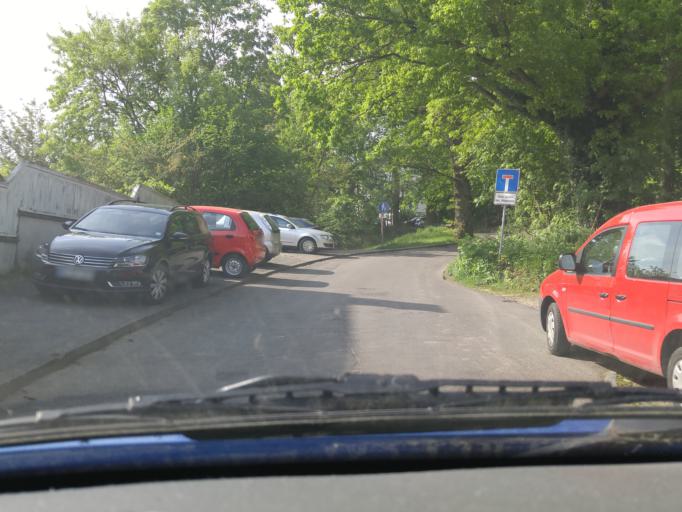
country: DE
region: Hesse
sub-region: Regierungsbezirk Darmstadt
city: Bad Nauheim
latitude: 50.3684
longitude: 8.7315
